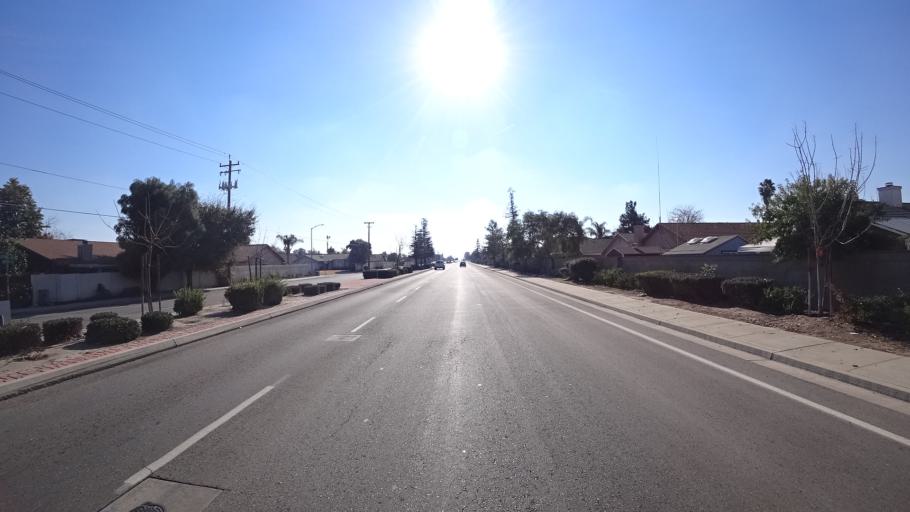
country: US
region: California
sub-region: Kern County
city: Greenfield
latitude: 35.3014
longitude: -119.0567
